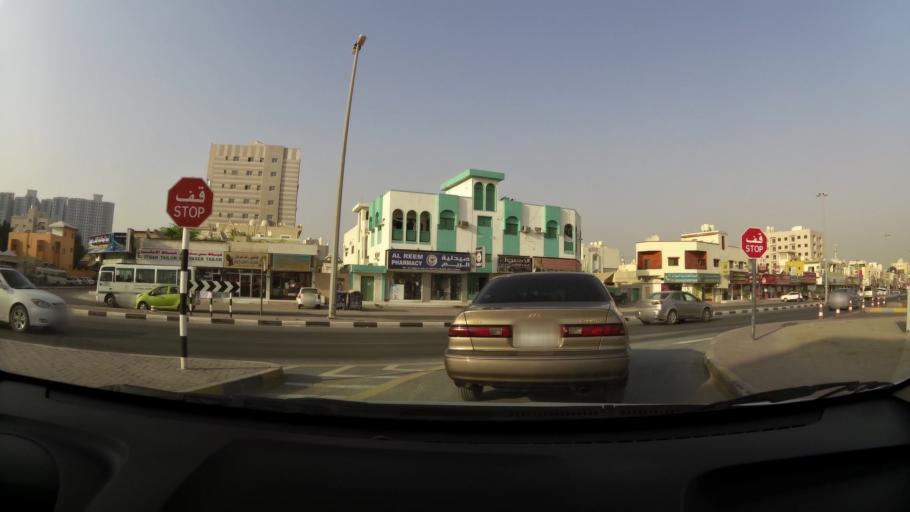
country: AE
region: Ajman
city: Ajman
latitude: 25.3851
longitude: 55.4415
